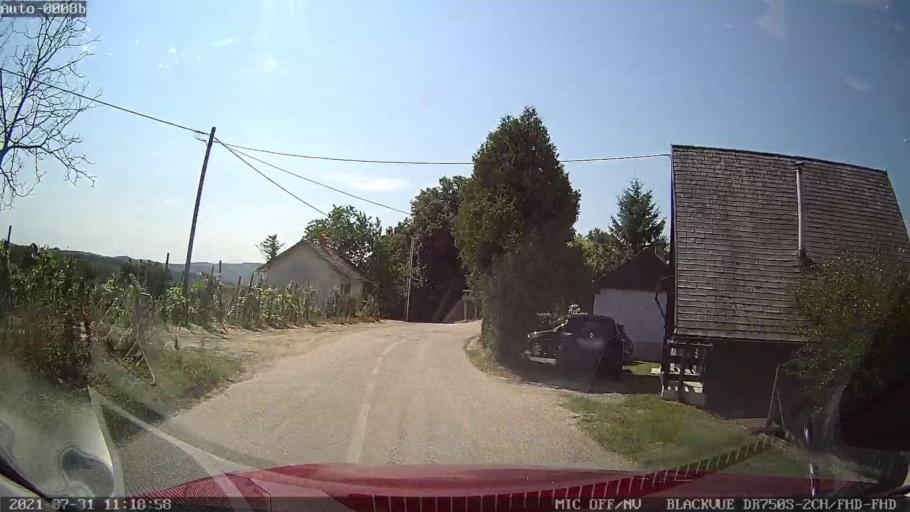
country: HR
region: Varazdinska
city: Jalzabet
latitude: 46.2420
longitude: 16.4753
